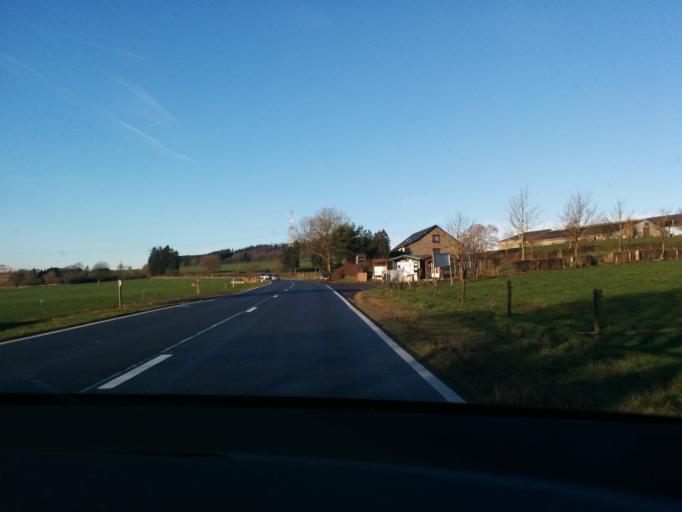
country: BE
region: Wallonia
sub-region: Province de Liege
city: Lierneux
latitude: 50.2618
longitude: 5.8366
